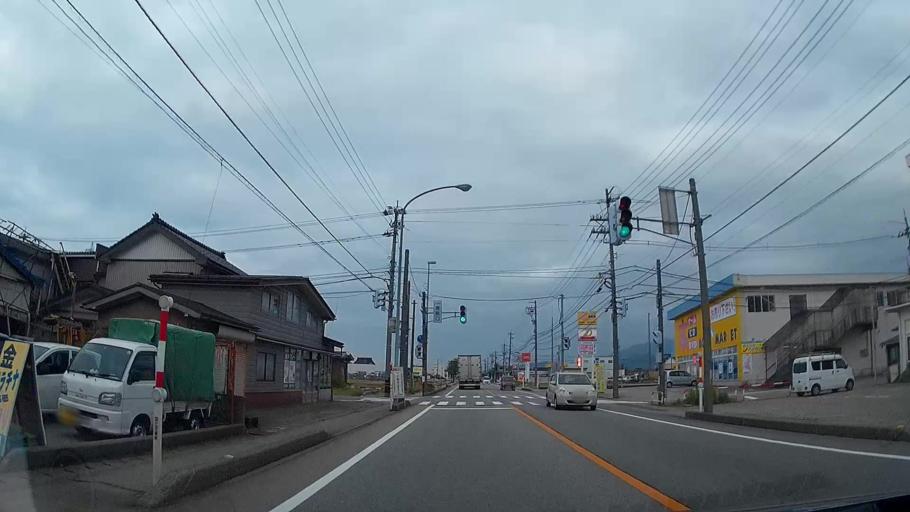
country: JP
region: Toyama
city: Nyuzen
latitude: 36.9367
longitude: 137.5080
